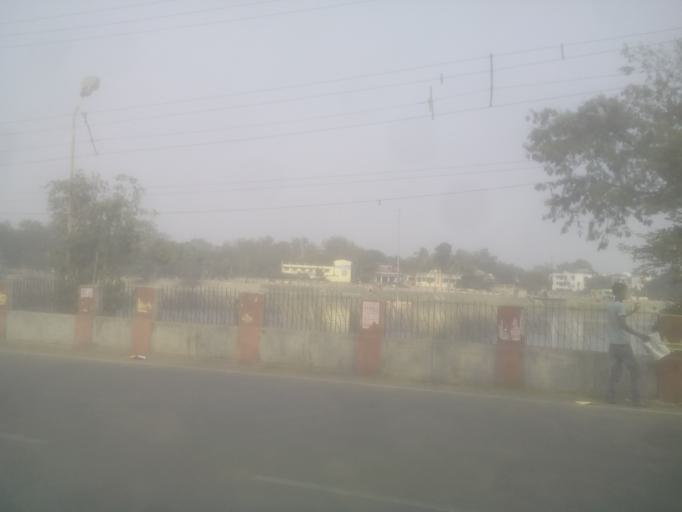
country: IN
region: Jharkhand
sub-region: Dhanbad
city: Dhanbad
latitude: 23.7997
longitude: 86.4277
